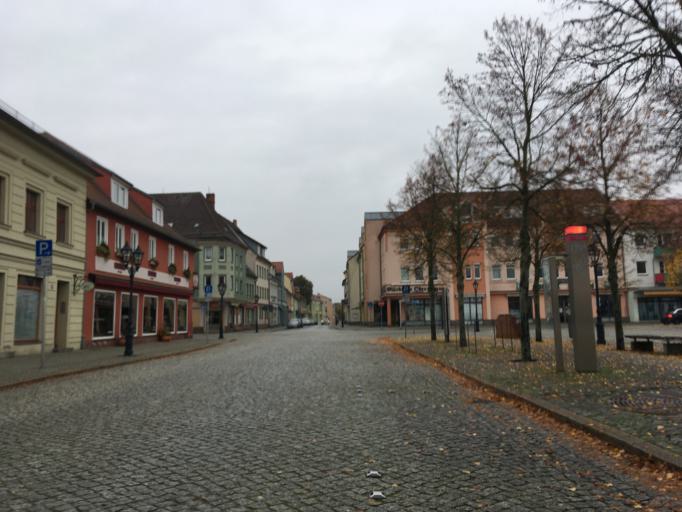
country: DE
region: Brandenburg
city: Beeskow
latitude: 52.1720
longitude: 14.2467
